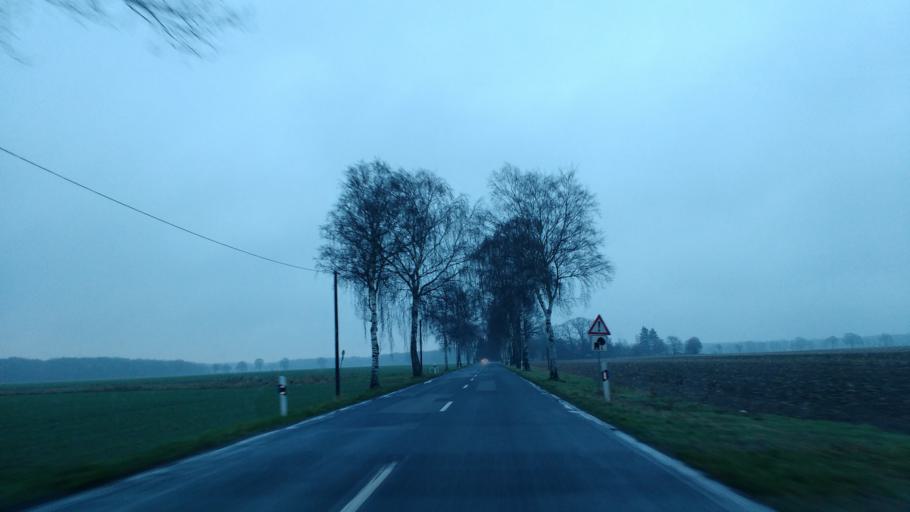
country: DE
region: Lower Saxony
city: Gilten
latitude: 52.6397
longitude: 9.5062
